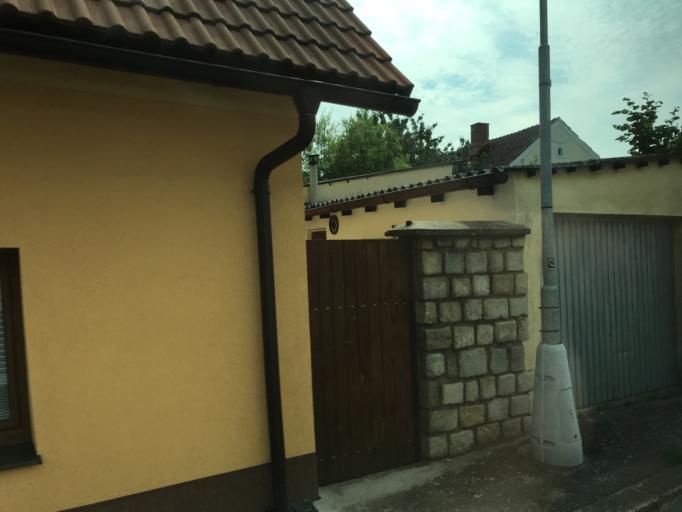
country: CZ
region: Jihocesky
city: Kamenny Ujezd
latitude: 48.8974
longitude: 14.4439
